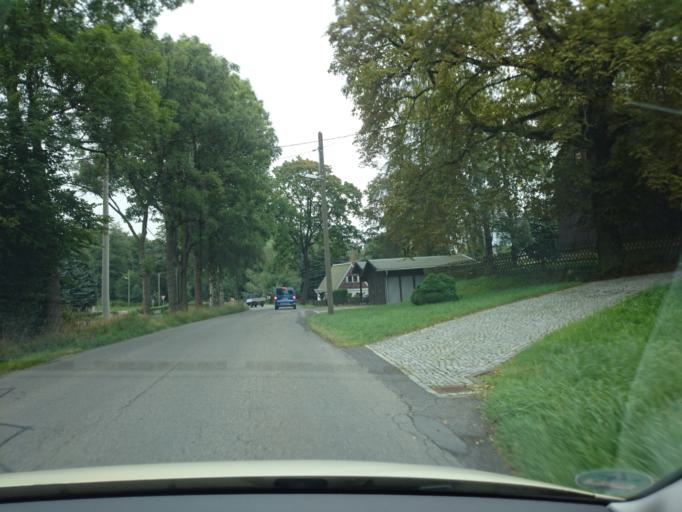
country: DE
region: Saxony
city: Eppendorf
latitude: 50.8030
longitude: 13.2452
